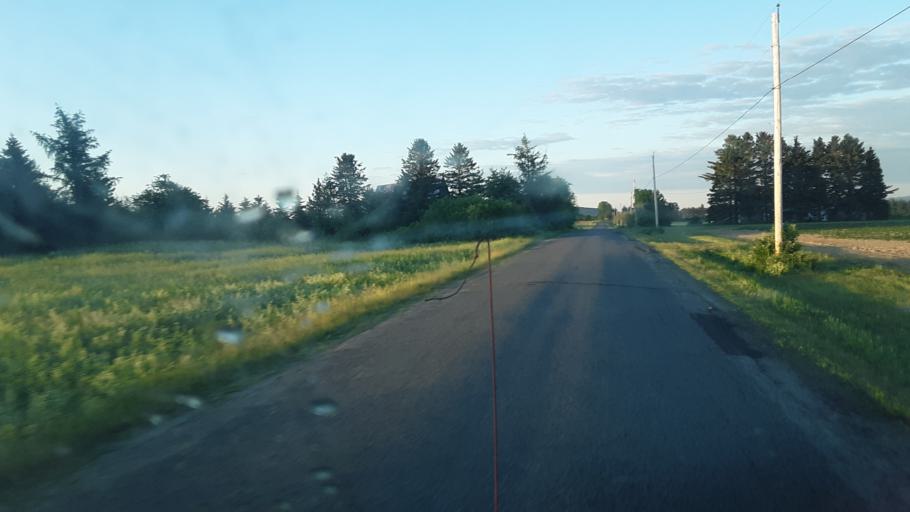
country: US
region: Maine
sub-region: Aroostook County
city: Caribou
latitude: 46.7857
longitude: -68.0990
